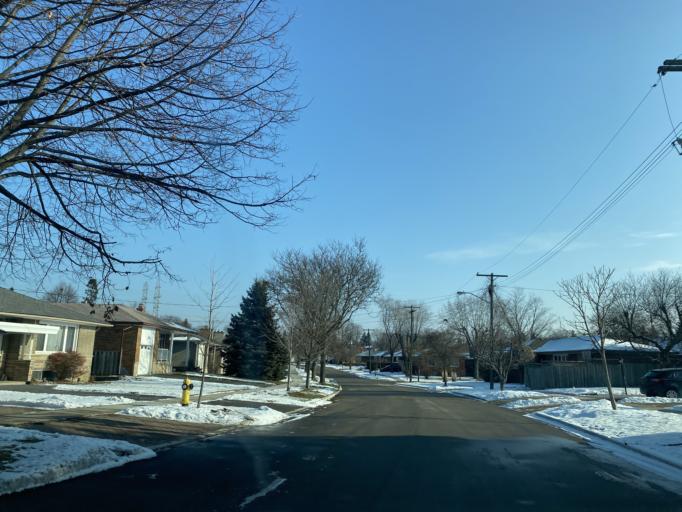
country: CA
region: Ontario
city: Etobicoke
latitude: 43.6712
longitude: -79.5675
